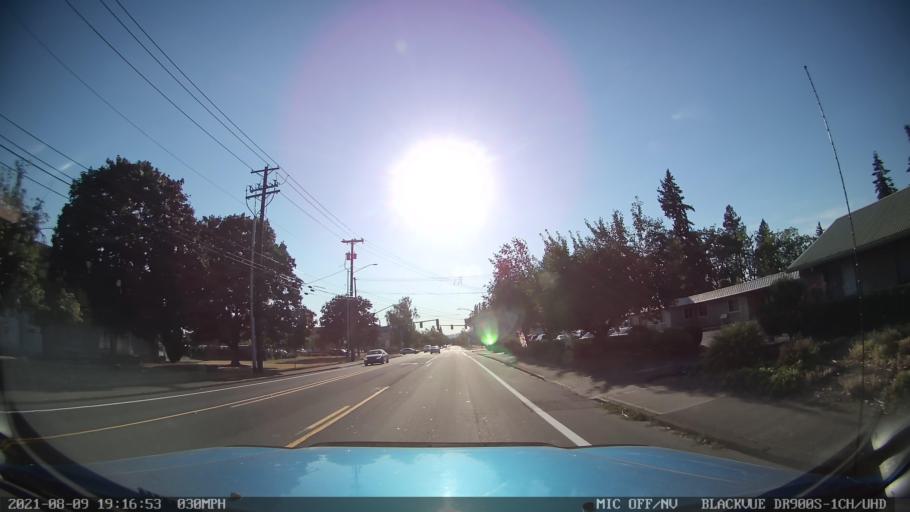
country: US
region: Oregon
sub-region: Marion County
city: Four Corners
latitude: 44.9399
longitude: -122.9986
